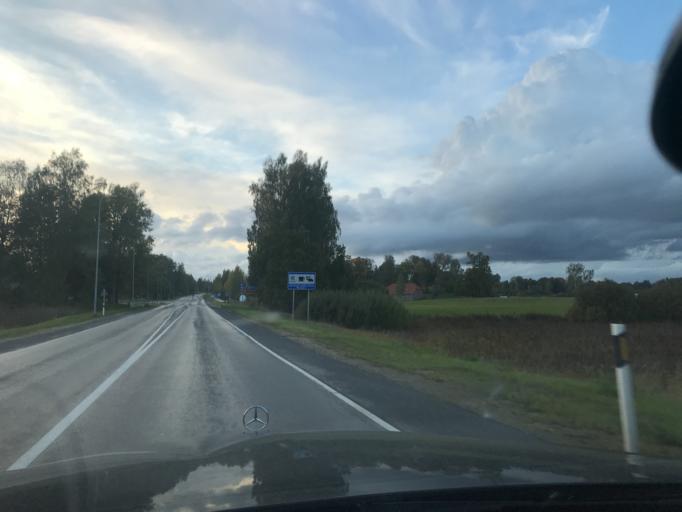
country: EE
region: Vorumaa
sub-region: Antsla vald
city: Vana-Antsla
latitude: 57.9259
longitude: 26.3362
